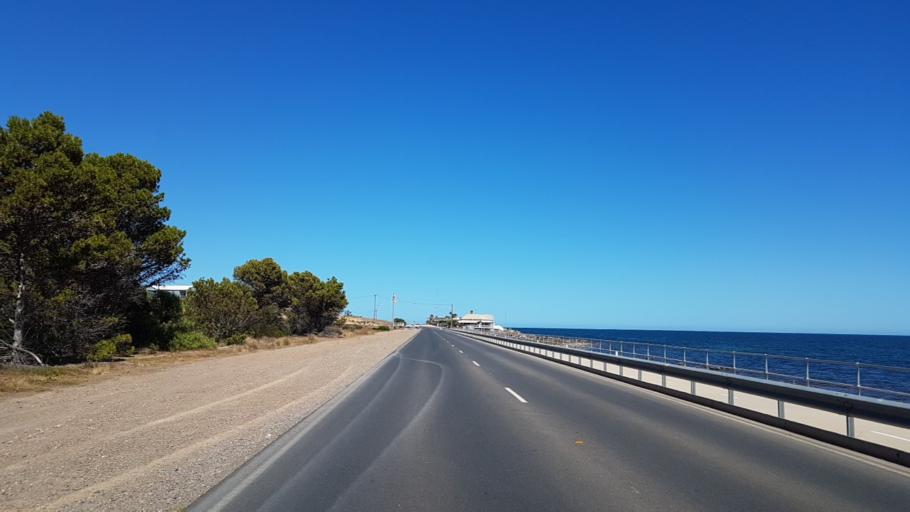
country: AU
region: South Australia
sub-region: Copper Coast
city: Wallaroo
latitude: -33.9294
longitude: 137.6182
